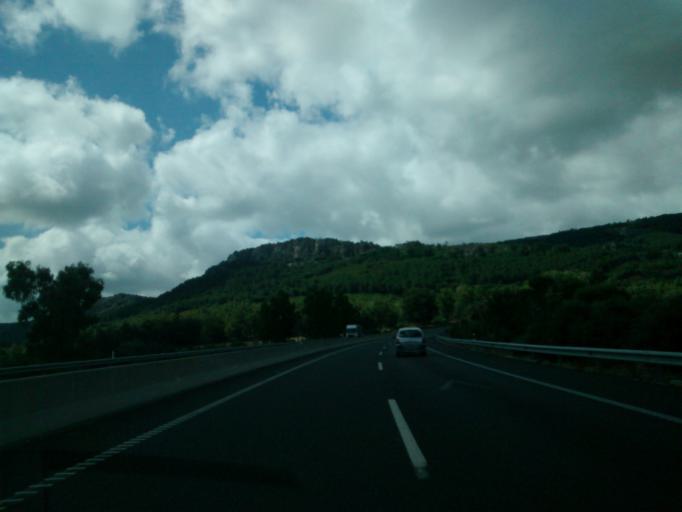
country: ES
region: Extremadura
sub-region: Provincia de Caceres
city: Higuera
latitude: 39.7040
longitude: -5.6895
